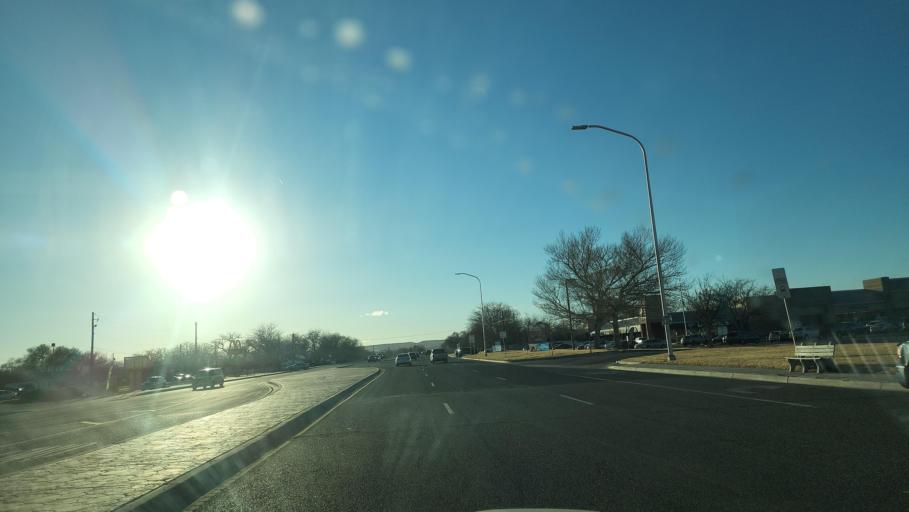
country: US
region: New Mexico
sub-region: Bernalillo County
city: South Valley
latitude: 35.0268
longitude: -106.6810
